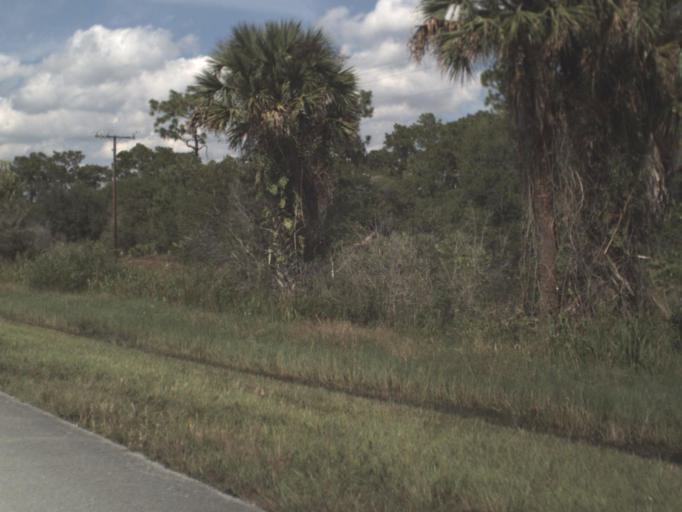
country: US
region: Florida
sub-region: Indian River County
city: Fellsmere
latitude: 27.5608
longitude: -80.8253
